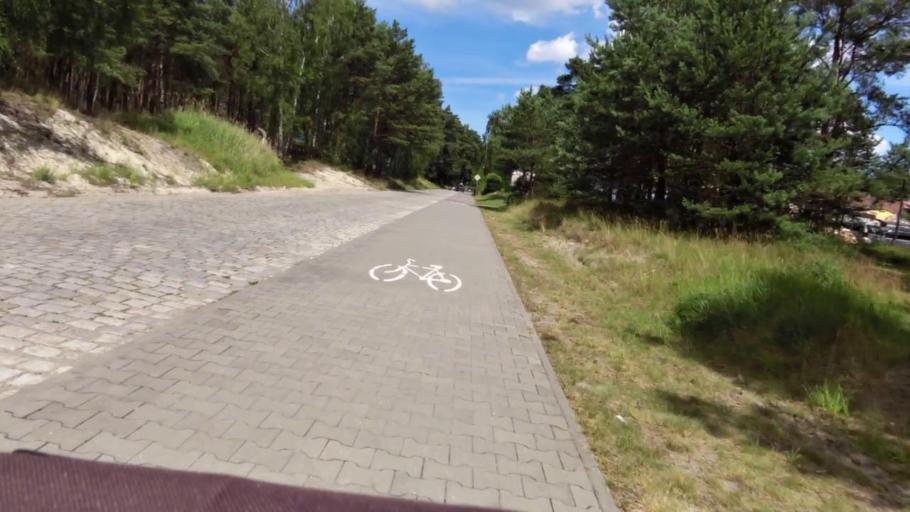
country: PL
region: West Pomeranian Voivodeship
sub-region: Powiat gryficki
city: Mrzezyno
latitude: 54.1383
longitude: 15.2756
